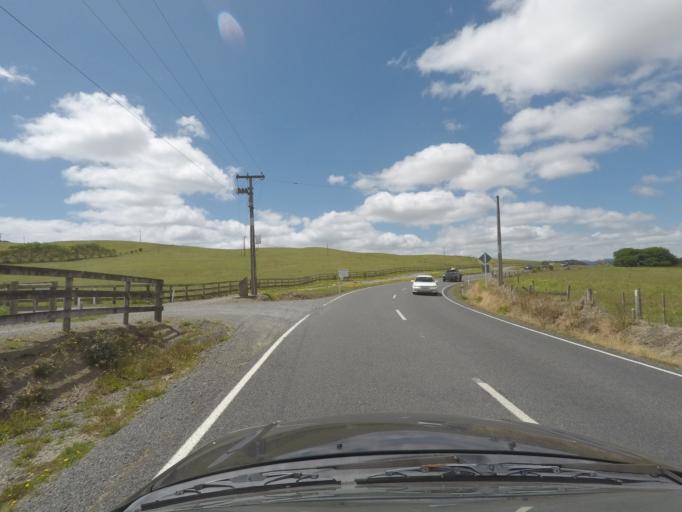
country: NZ
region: Northland
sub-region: Whangarei
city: Ruakaka
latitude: -35.9877
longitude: 174.4563
